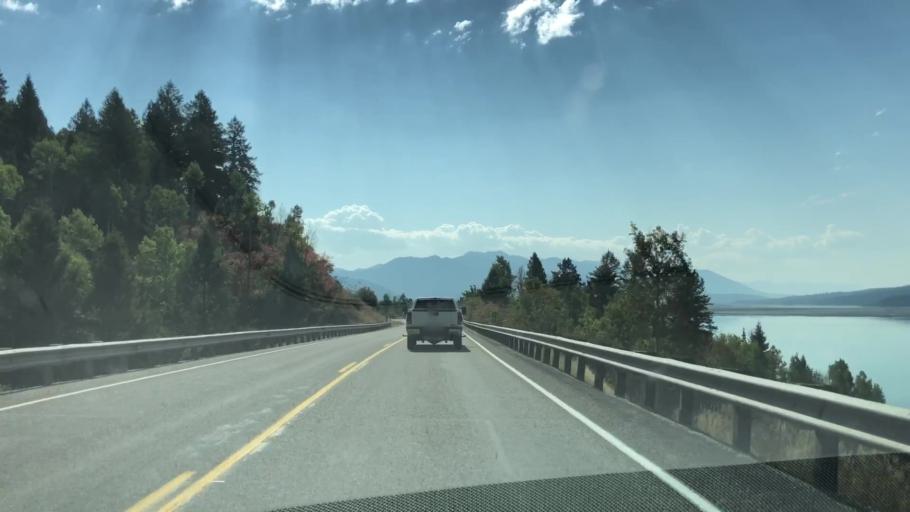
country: US
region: Wyoming
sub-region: Teton County
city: Hoback
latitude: 43.2296
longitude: -111.0885
